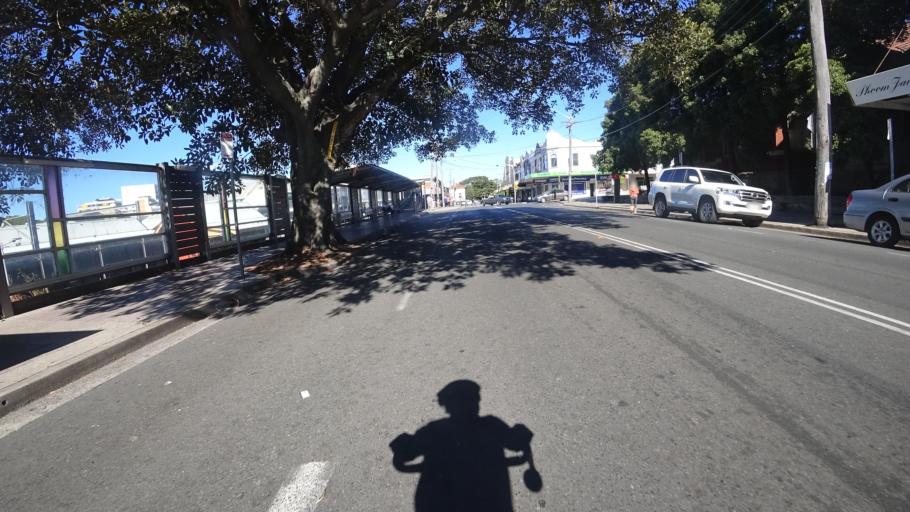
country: AU
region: New South Wales
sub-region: Rockdale
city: Banksia
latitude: -33.9515
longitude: 151.1366
